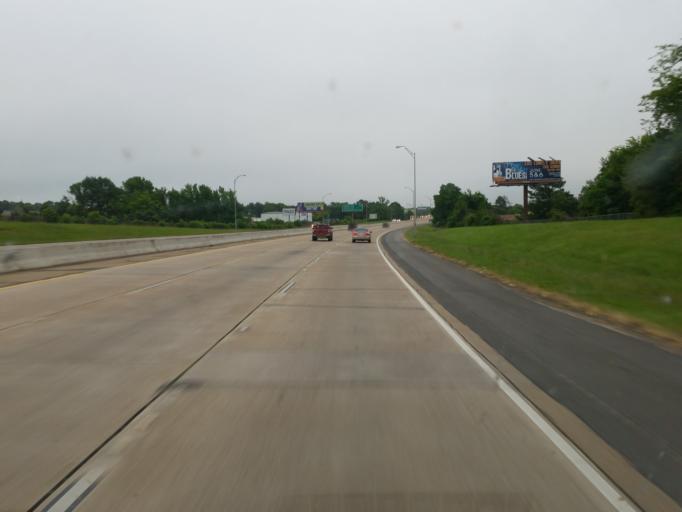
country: US
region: Louisiana
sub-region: Caddo Parish
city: Shreveport
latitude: 32.4664
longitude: -93.8147
